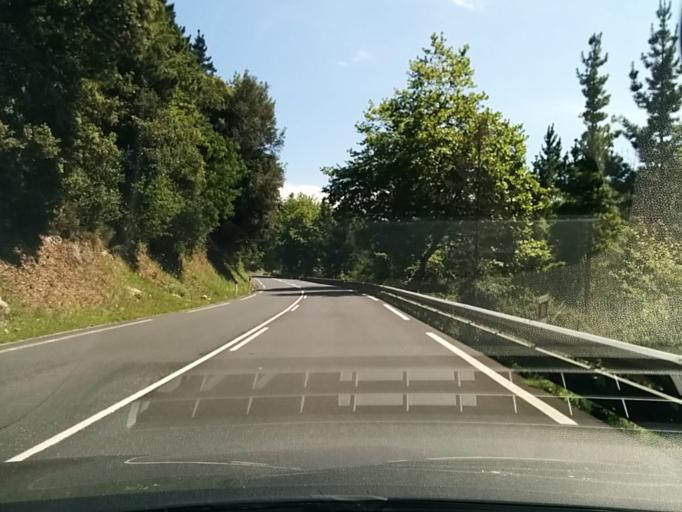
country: ES
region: Basque Country
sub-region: Provincia de Guipuzcoa
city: Deba
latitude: 43.2834
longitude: -2.3119
